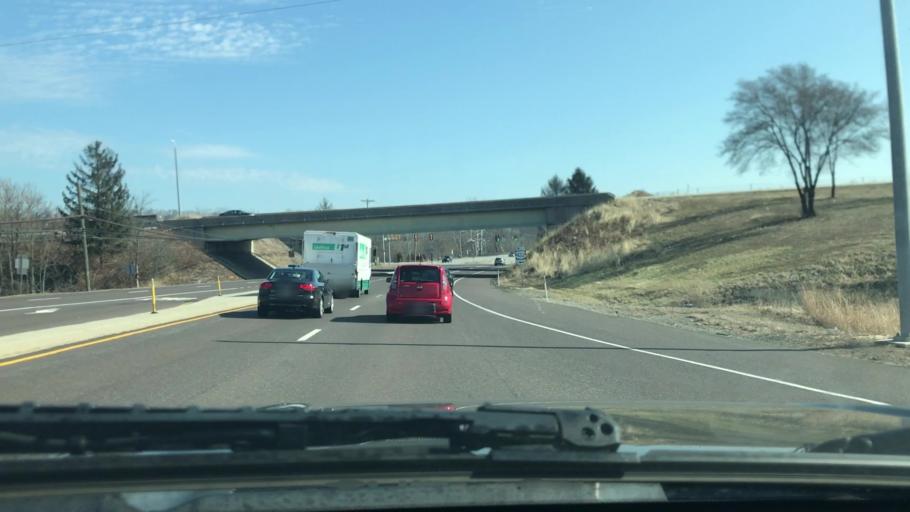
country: US
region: Pennsylvania
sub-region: Montgomery County
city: Audubon
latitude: 40.1341
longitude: -75.4484
